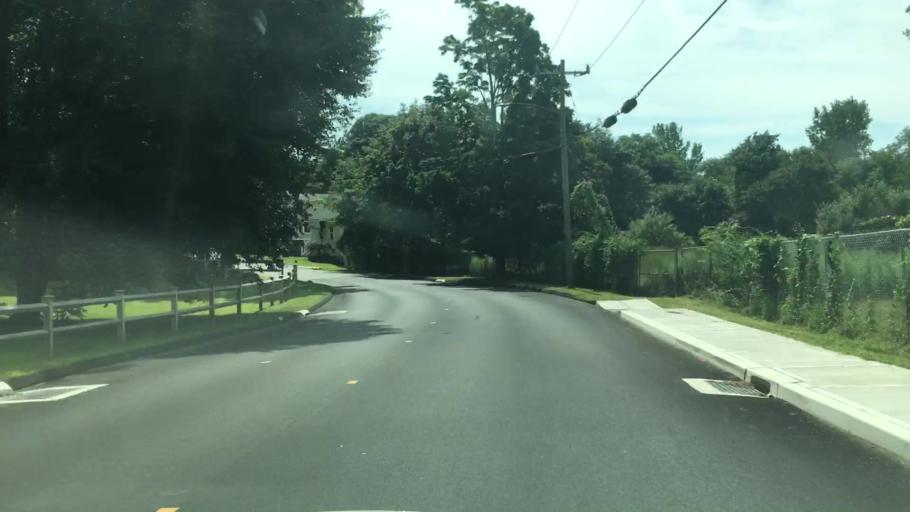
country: US
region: Connecticut
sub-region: Middlesex County
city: Deep River Center
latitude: 41.3457
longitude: -72.4469
